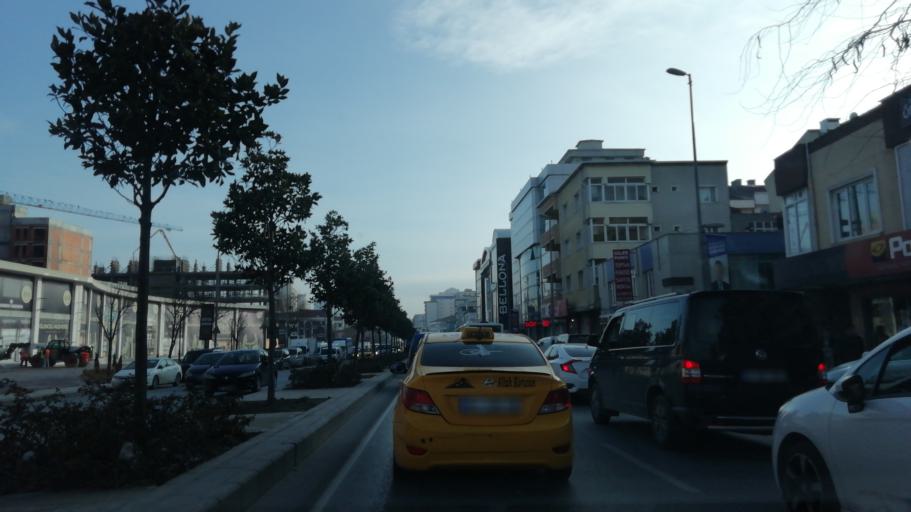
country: TR
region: Istanbul
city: Esenyurt
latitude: 41.0456
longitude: 28.6748
